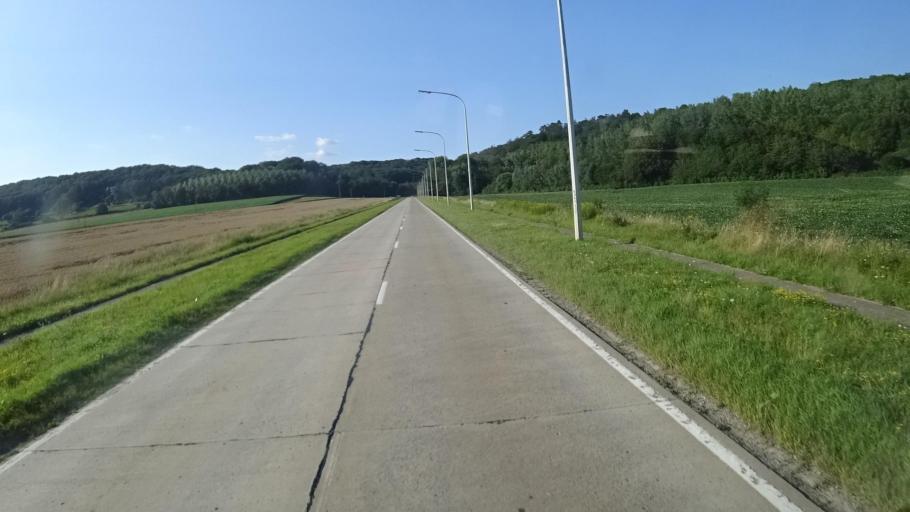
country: BE
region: Wallonia
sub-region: Province de Namur
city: Floreffe
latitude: 50.4592
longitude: 4.7681
